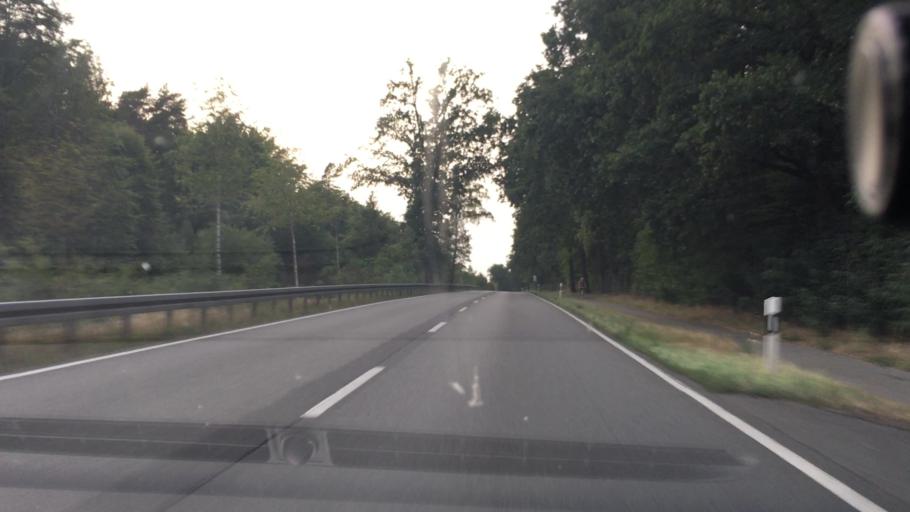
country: DE
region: Lower Saxony
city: Linsburg
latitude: 52.5654
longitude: 9.3222
